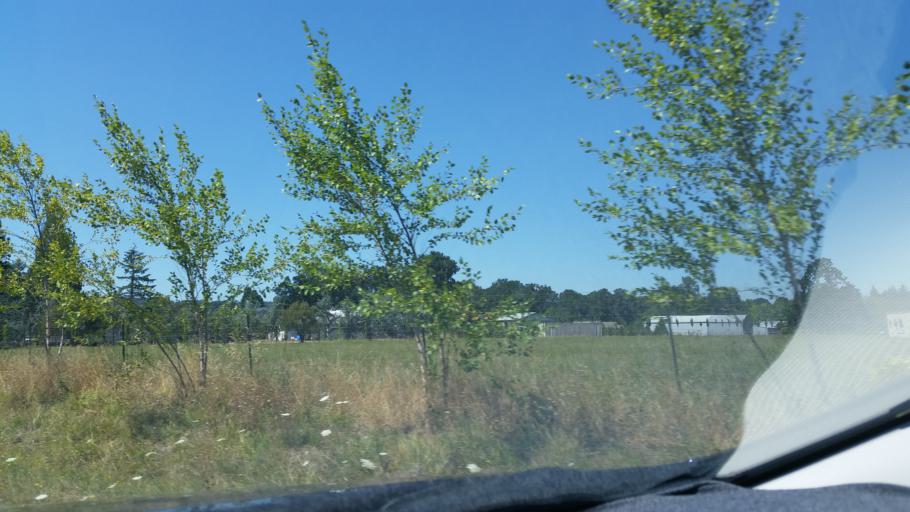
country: US
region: Oregon
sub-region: Clackamas County
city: Wilsonville
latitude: 45.2596
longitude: -122.8342
